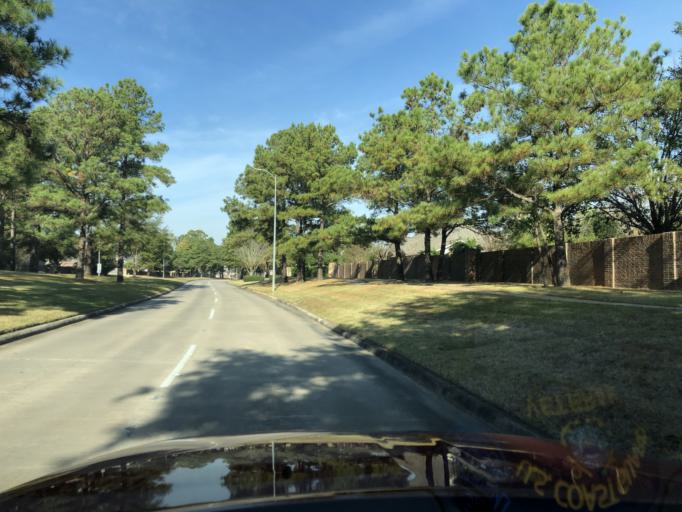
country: US
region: Texas
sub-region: Harris County
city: Tomball
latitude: 30.0296
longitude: -95.5643
